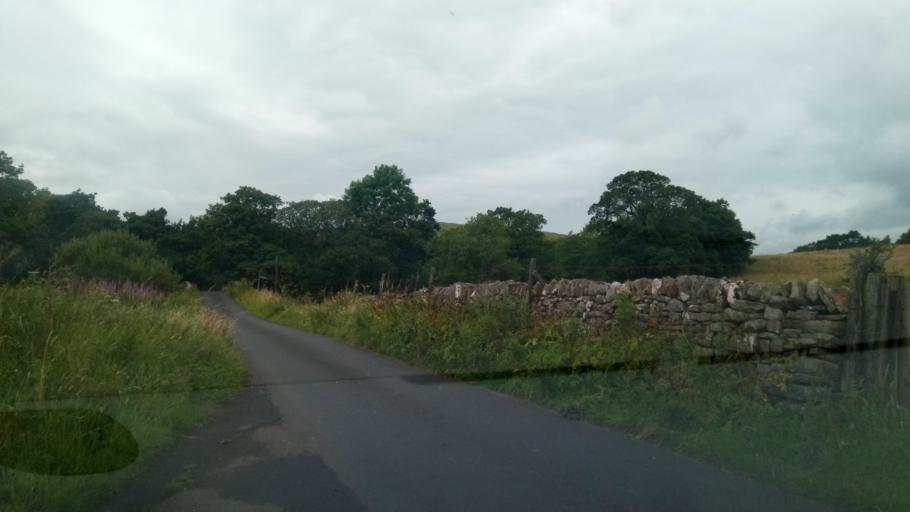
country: GB
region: England
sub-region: Cumbria
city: Kirkby Stephen
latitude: 54.4198
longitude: -2.3378
